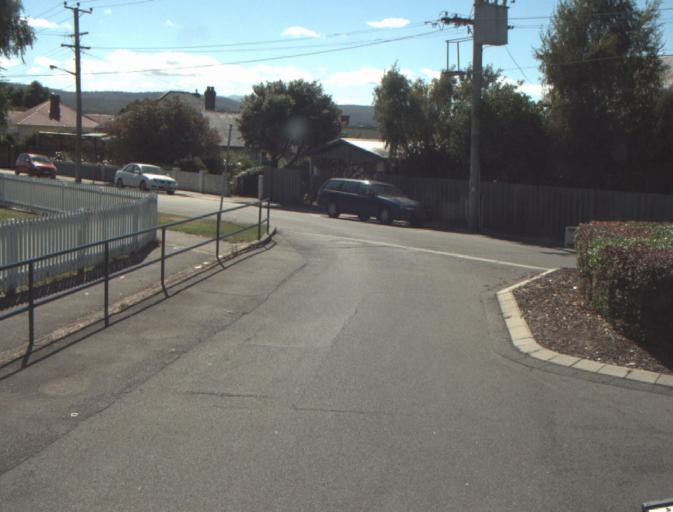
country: AU
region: Tasmania
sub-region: Launceston
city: Newnham
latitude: -41.4088
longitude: 147.1296
